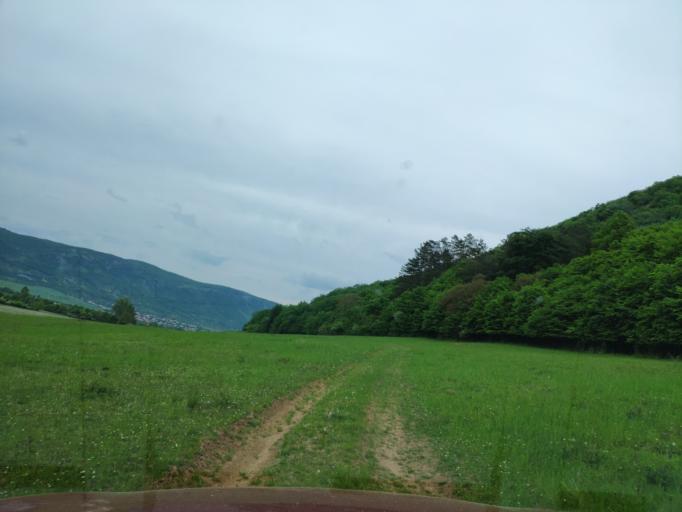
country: SK
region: Kosicky
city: Roznava
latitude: 48.5693
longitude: 20.6476
